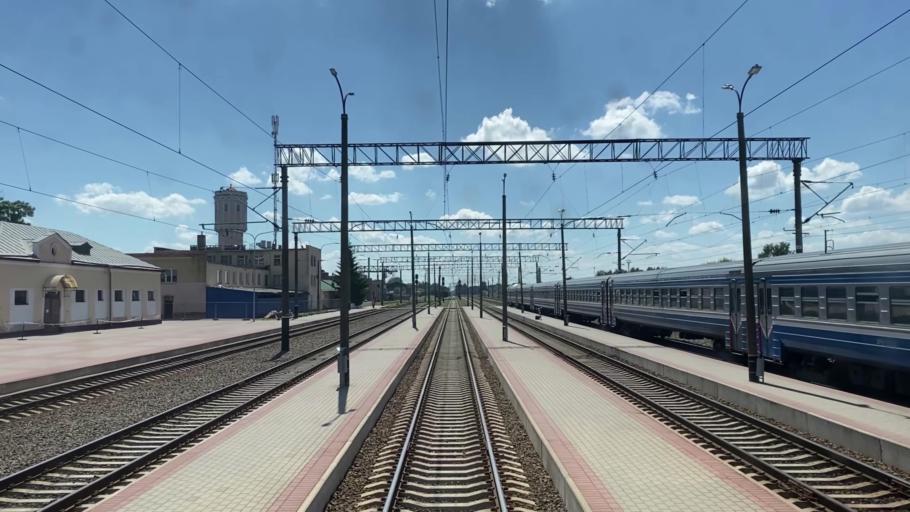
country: BY
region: Brest
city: Baranovichi
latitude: 53.1292
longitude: 26.0423
